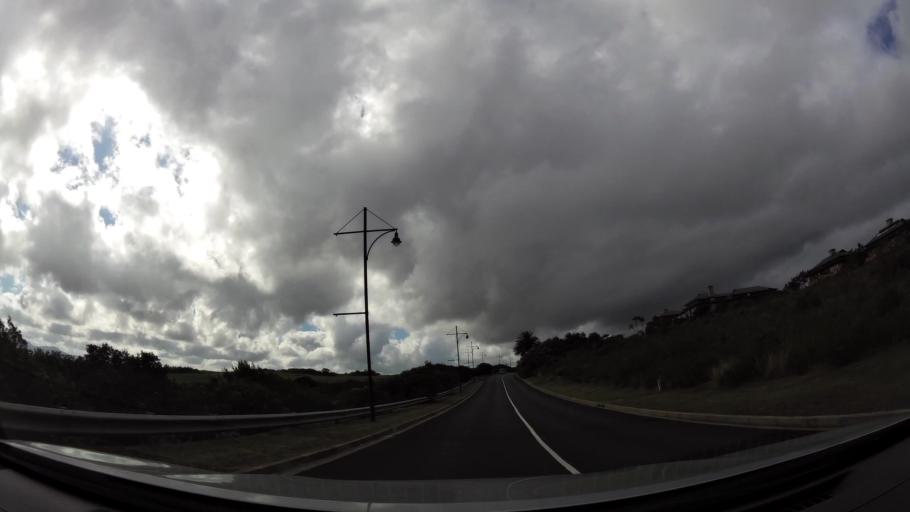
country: ZA
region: Western Cape
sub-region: Eden District Municipality
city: Knysna
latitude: -34.0697
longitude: 23.0877
